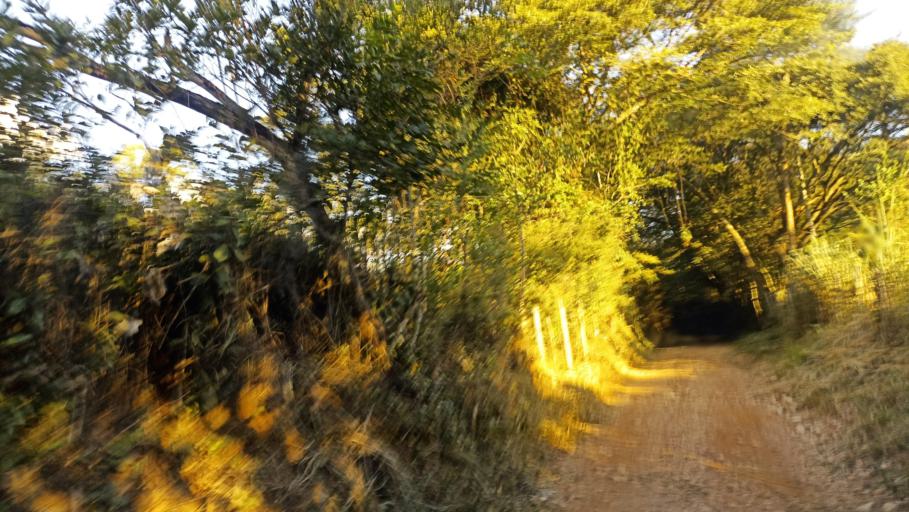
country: BR
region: Minas Gerais
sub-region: Sao Joao Del Rei
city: Sao Joao del Rei
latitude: -21.1791
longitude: -44.3557
